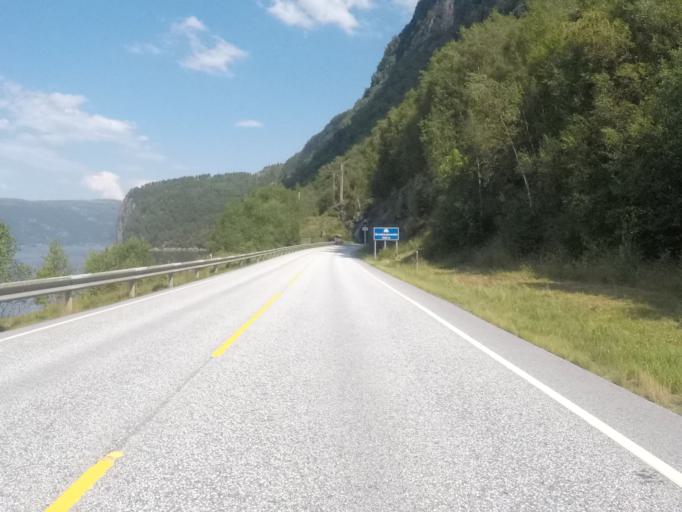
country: NO
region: Sogn og Fjordane
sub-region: Hyllestad
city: Hyllestad
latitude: 61.0315
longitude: 5.4880
